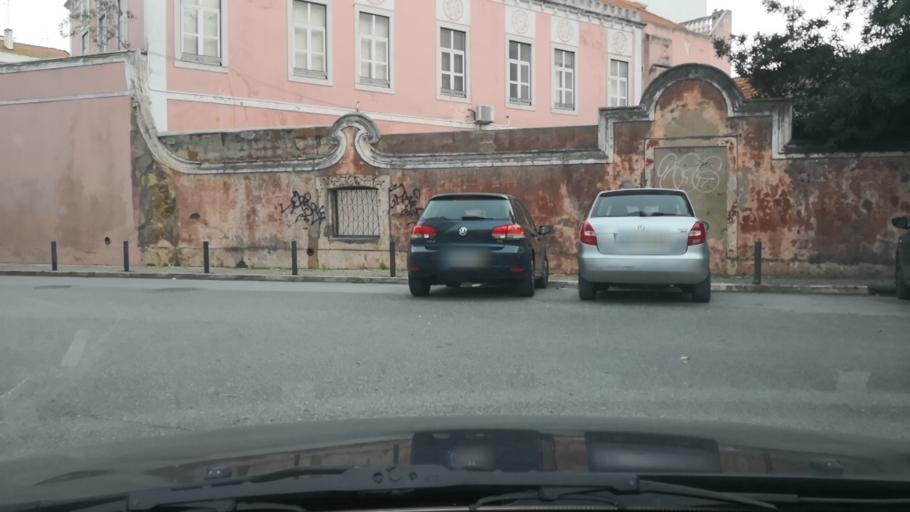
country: PT
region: Setubal
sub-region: Setubal
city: Setubal
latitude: 38.5255
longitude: -8.8977
